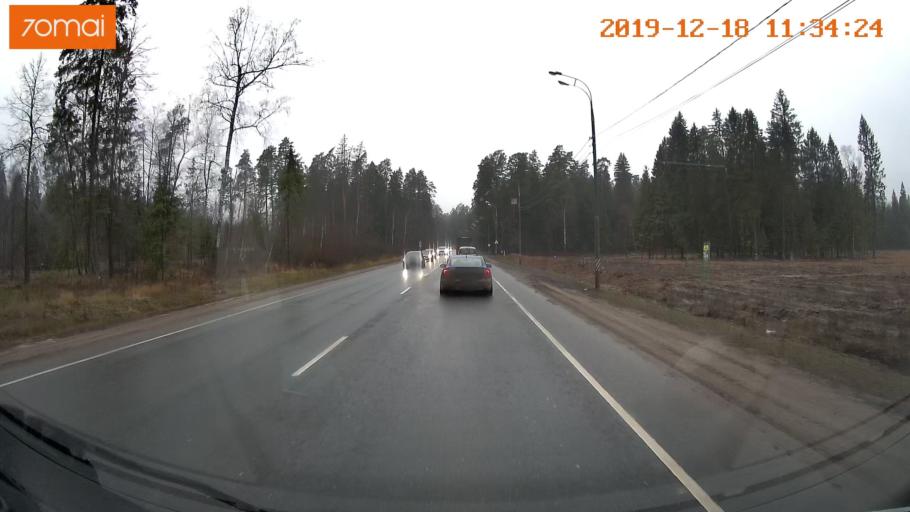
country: RU
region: Moskovskaya
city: Bol'shiye Vyazemy
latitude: 55.6753
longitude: 36.9331
